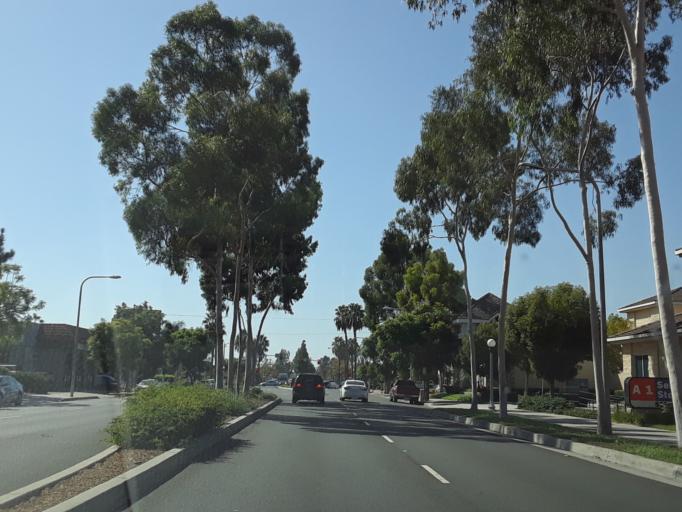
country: US
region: California
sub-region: Orange County
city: La Palma
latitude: 33.8318
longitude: -118.0436
